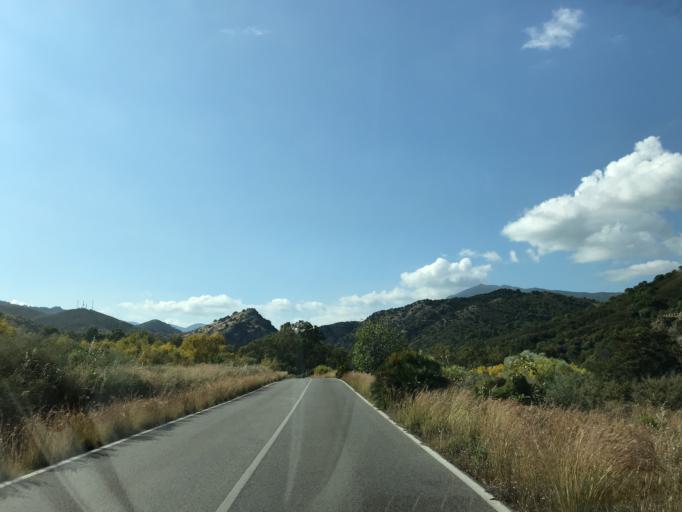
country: ES
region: Andalusia
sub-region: Provincia de Malaga
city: Benahavis
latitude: 36.5028
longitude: -5.0277
